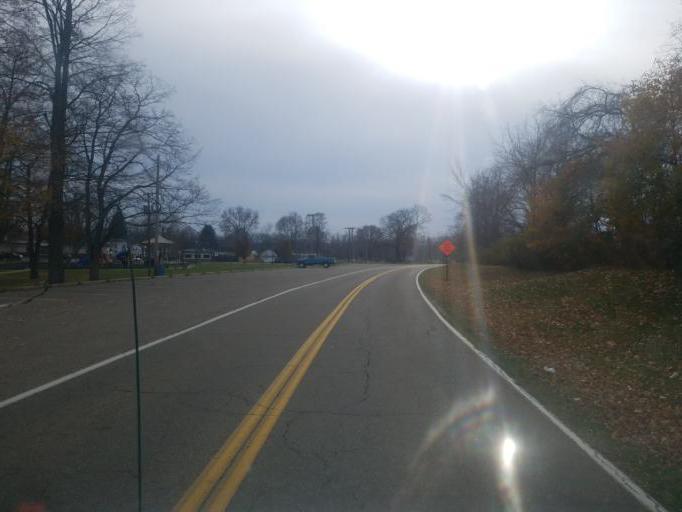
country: US
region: Ohio
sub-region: Knox County
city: Mount Vernon
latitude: 40.3958
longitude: -82.5021
